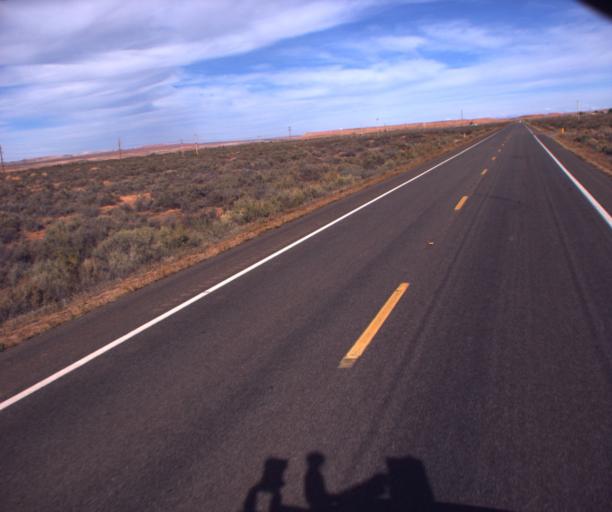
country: US
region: Arizona
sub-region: Navajo County
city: Kayenta
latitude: 36.8085
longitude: -109.9056
